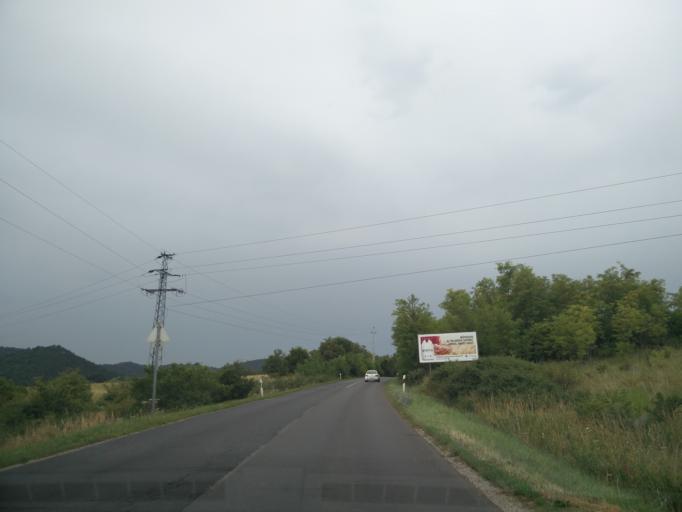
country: HU
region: Pest
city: Budakeszi
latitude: 47.4816
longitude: 18.9058
